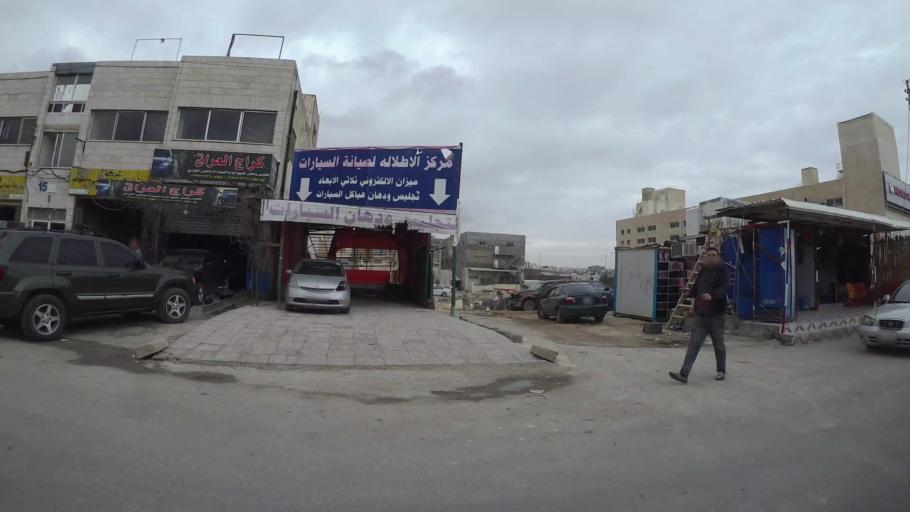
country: JO
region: Amman
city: Wadi as Sir
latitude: 31.9433
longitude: 35.8447
